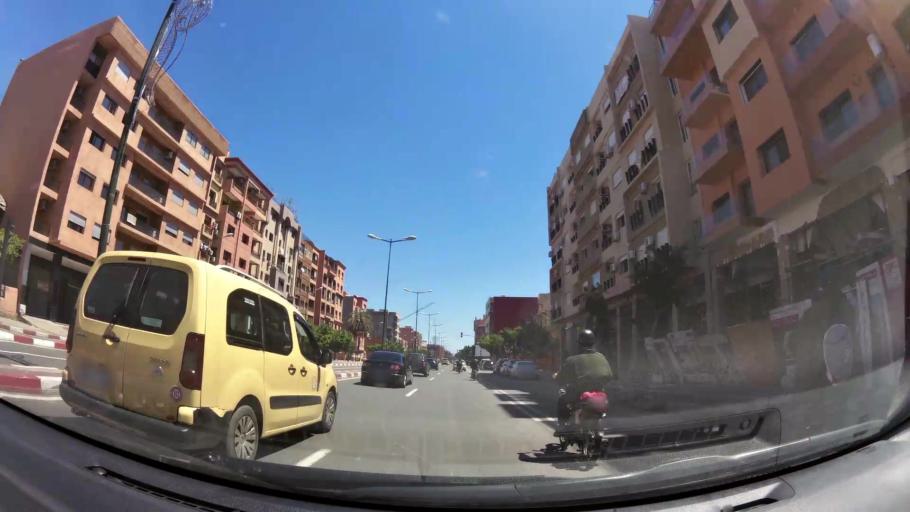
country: MA
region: Marrakech-Tensift-Al Haouz
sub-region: Marrakech
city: Marrakesh
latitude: 31.6307
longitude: -8.0138
